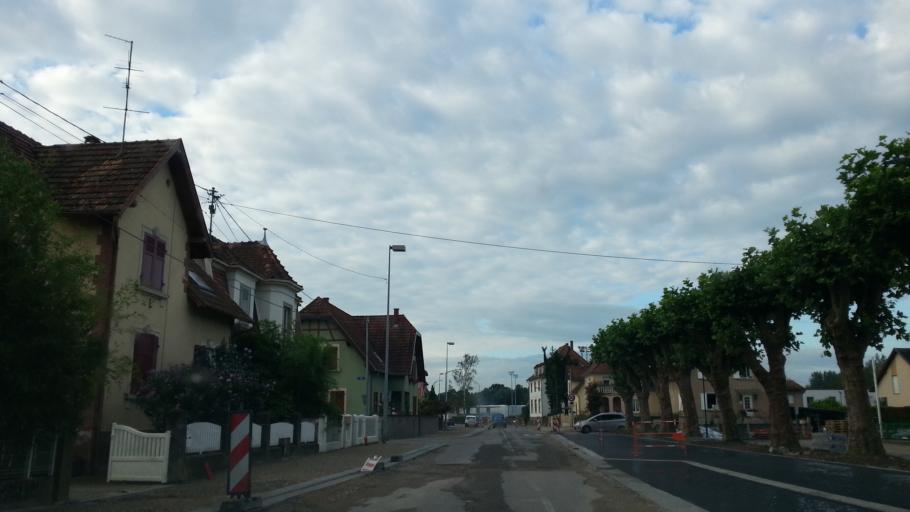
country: FR
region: Alsace
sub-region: Departement du Bas-Rhin
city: Erstein
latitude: 48.4161
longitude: 7.6660
